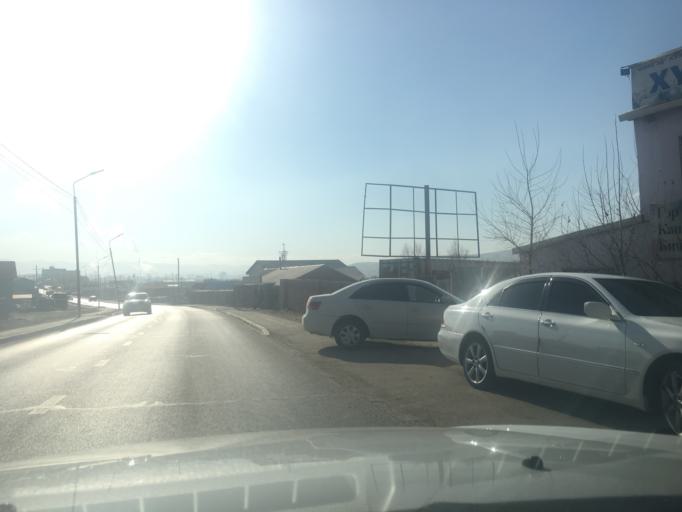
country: MN
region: Ulaanbaatar
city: Ulaanbaatar
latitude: 47.9604
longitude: 106.8272
